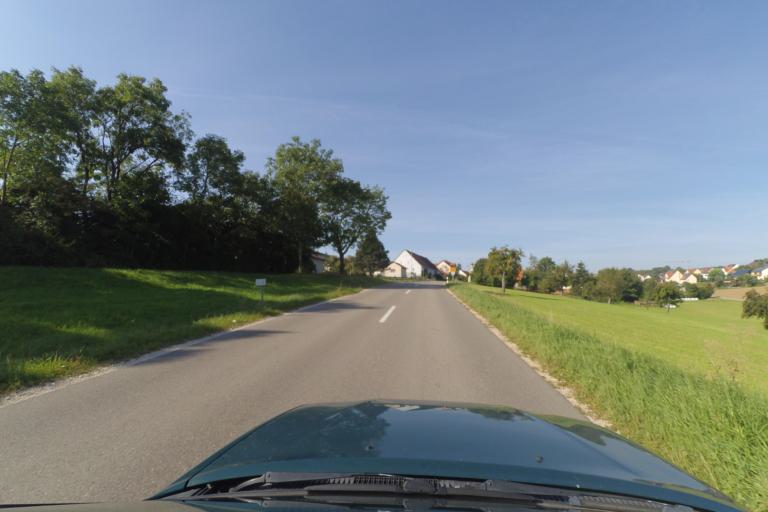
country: DE
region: Bavaria
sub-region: Swabia
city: Genderkingen
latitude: 48.7433
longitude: 10.8891
